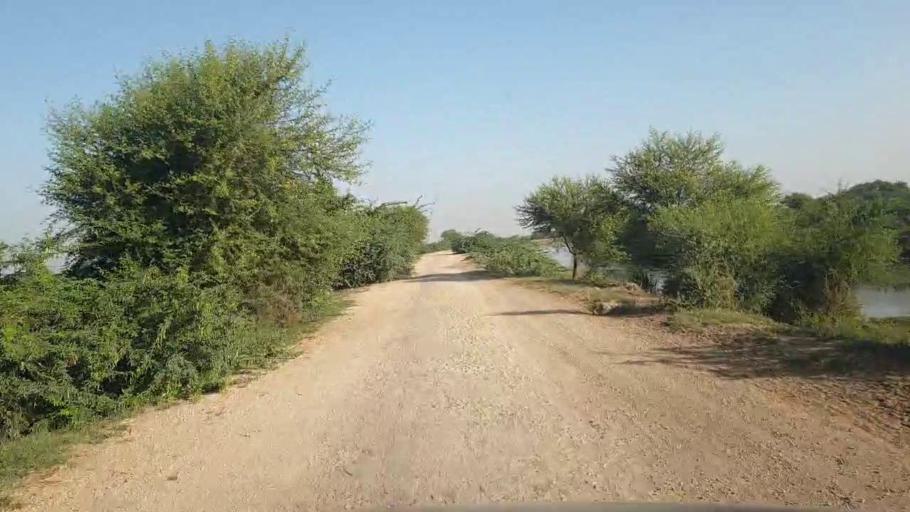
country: PK
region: Sindh
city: Badin
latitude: 24.6936
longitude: 68.8160
